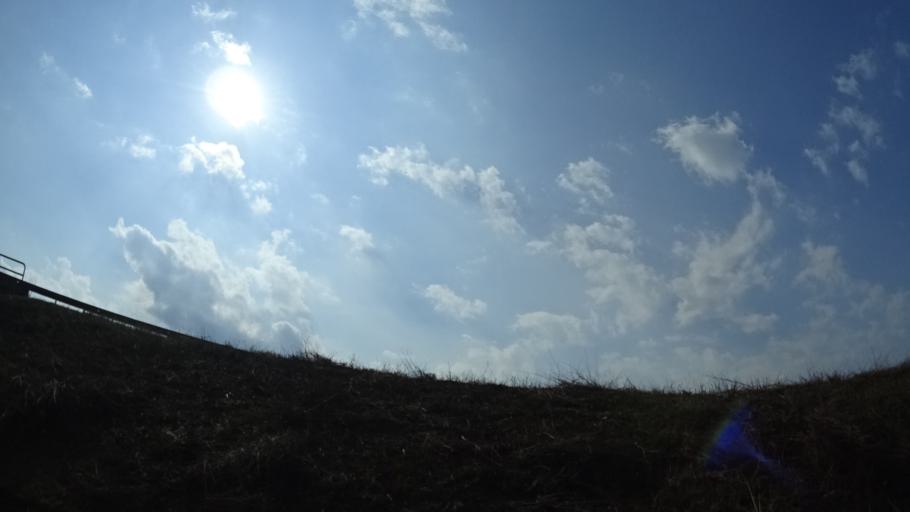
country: DE
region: Bavaria
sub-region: Regierungsbezirk Unterfranken
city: Wiesentheid
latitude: 49.7746
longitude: 10.3641
